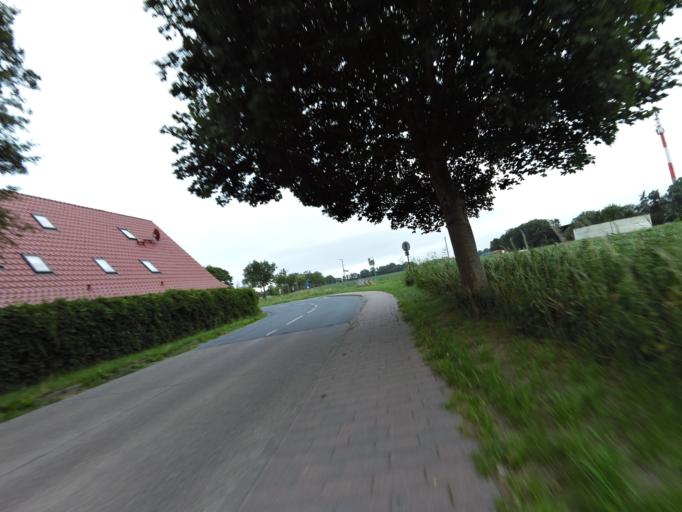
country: DE
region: Lower Saxony
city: Padingbuttel
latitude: 53.7241
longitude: 8.5381
